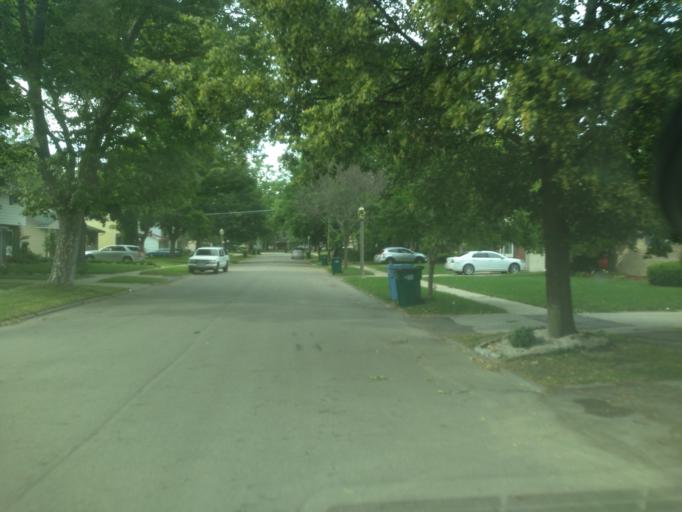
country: US
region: Michigan
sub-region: Eaton County
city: Waverly
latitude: 42.6934
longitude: -84.5940
